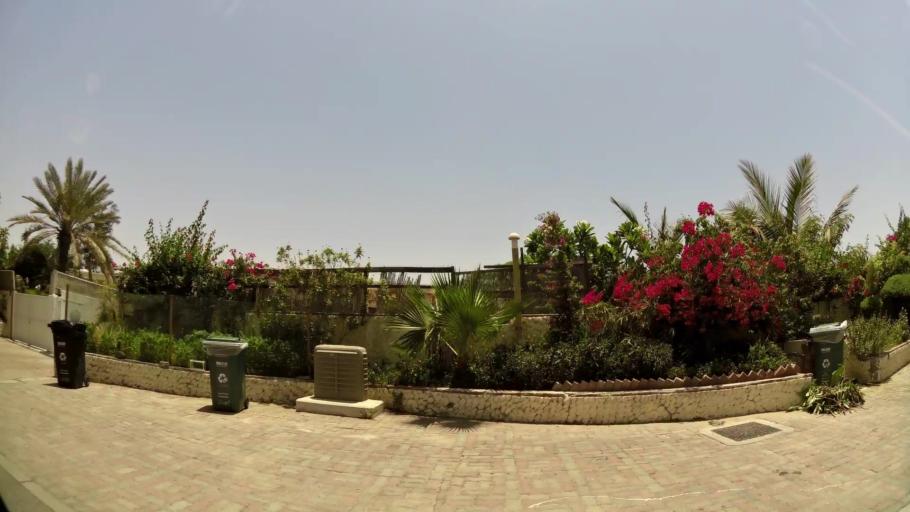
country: AE
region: Dubai
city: Dubai
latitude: 25.2197
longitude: 55.2564
